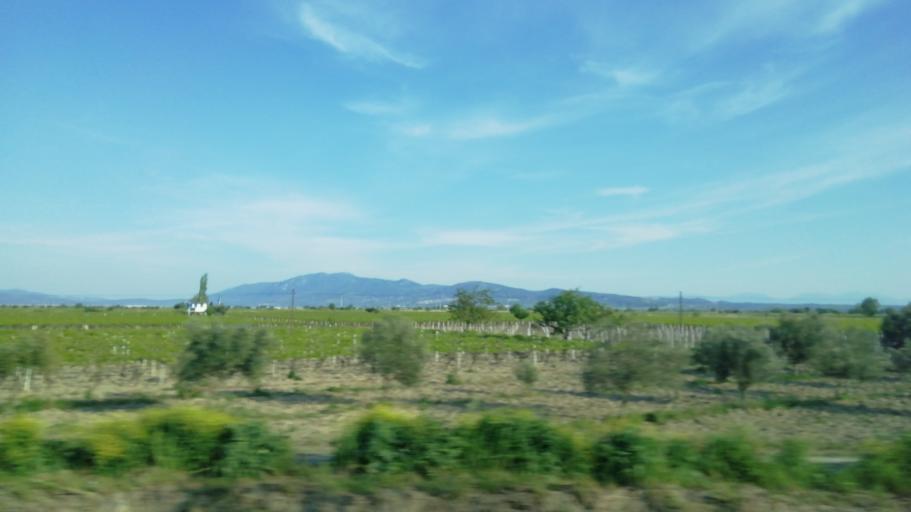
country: TR
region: Manisa
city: Saruhanli
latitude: 38.7514
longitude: 27.6245
